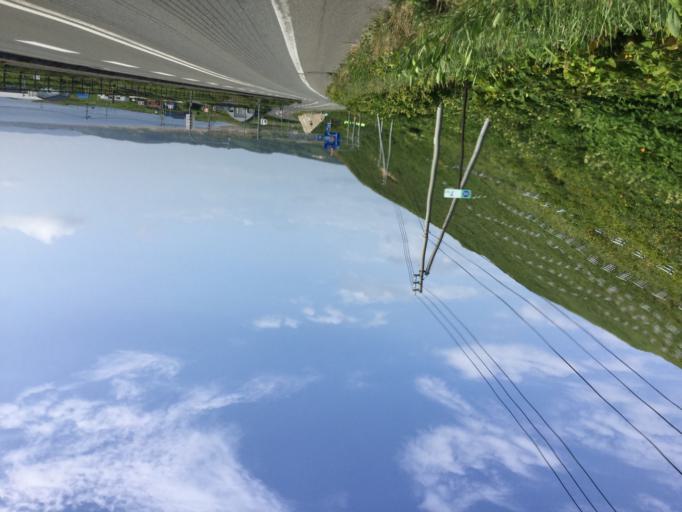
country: JP
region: Hokkaido
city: Wakkanai
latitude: 45.3761
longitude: 141.6552
